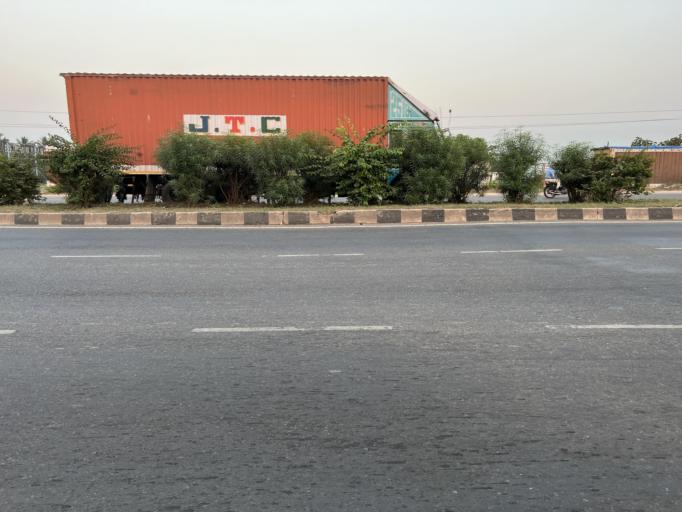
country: IN
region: Odisha
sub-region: Khordha
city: Bhubaneshwar
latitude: 20.3301
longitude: 85.8840
